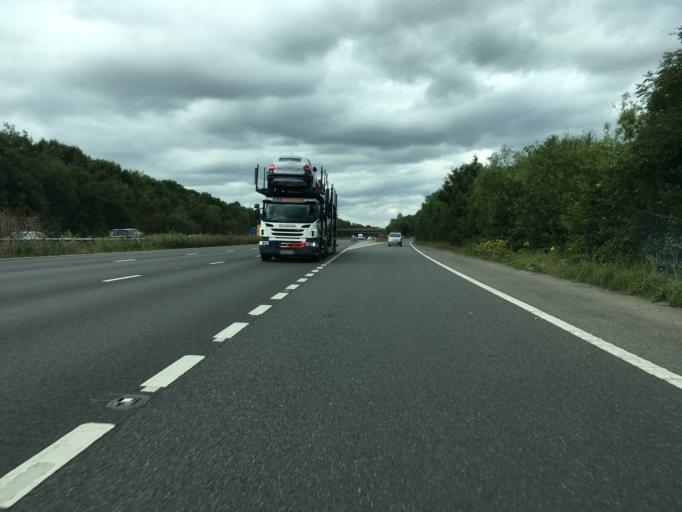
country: GB
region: England
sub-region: West Sussex
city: Maidenbower
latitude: 51.1281
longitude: -0.1417
